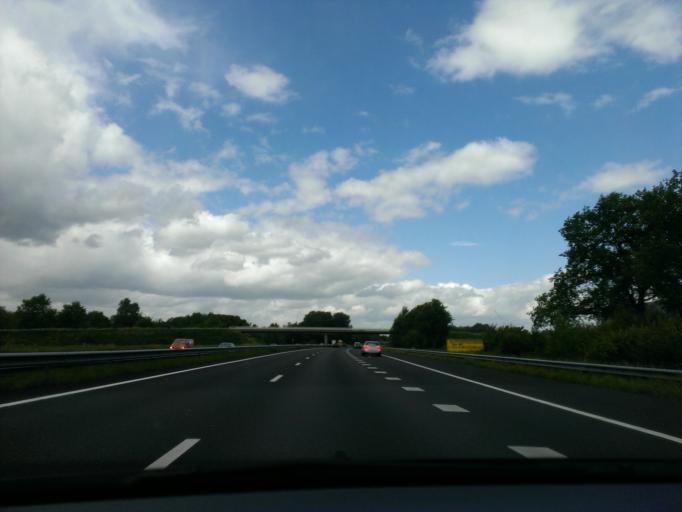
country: NL
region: Limburg
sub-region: Gemeente Venray
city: Venray
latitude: 51.5151
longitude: 6.0073
